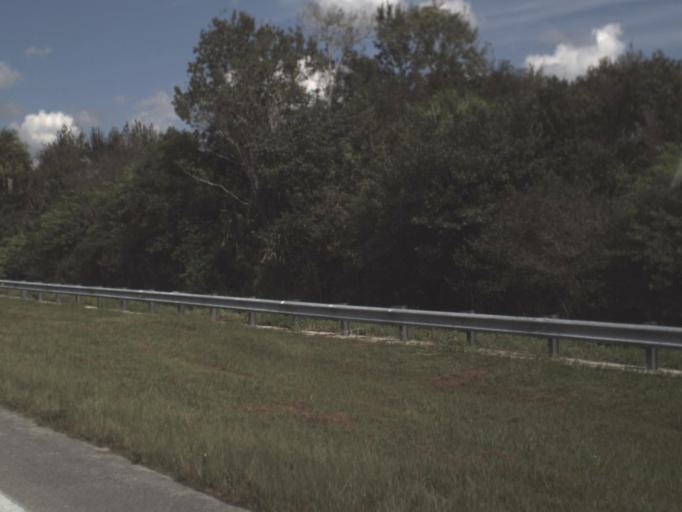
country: US
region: Florida
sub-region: Collier County
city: Orangetree
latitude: 26.1183
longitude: -81.3448
